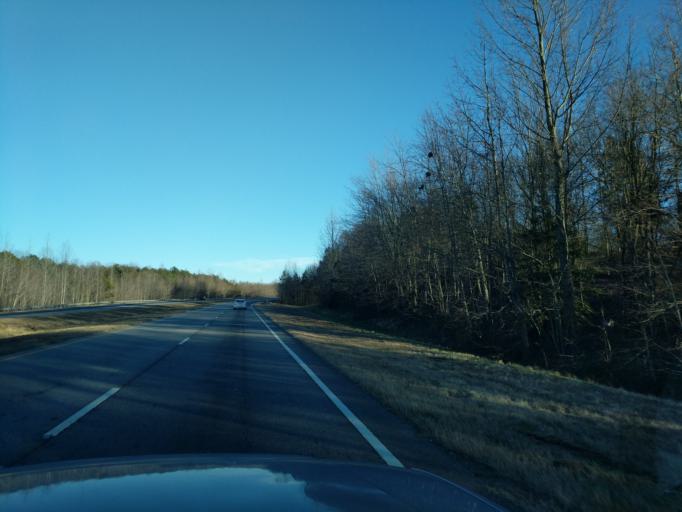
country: US
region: Georgia
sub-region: Stephens County
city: Toccoa
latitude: 34.5932
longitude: -83.4224
